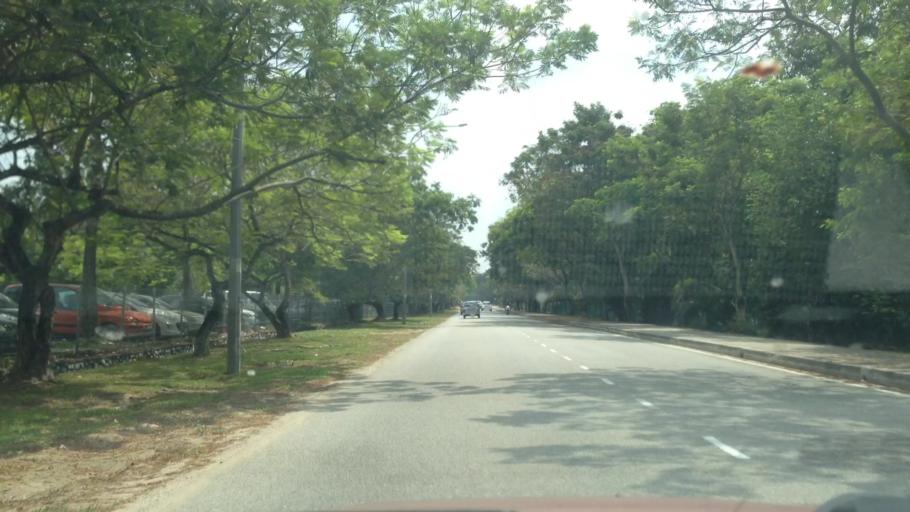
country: MY
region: Selangor
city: Subang Jaya
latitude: 3.0525
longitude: 101.5739
